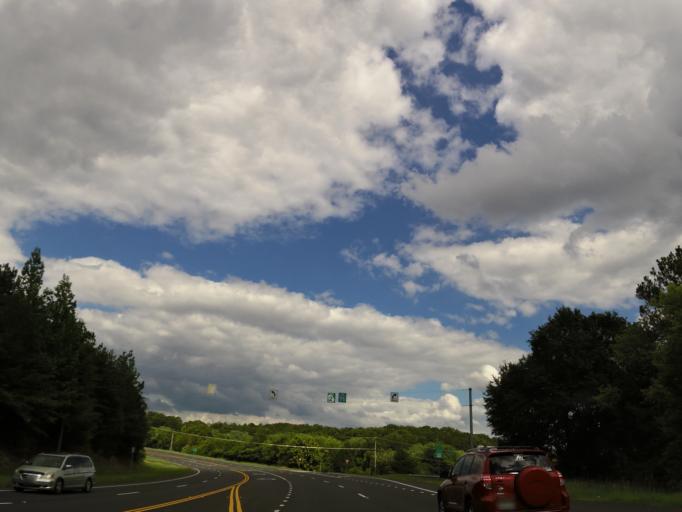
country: US
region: Georgia
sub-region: Walker County
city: Fairview
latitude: 34.9464
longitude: -85.2843
